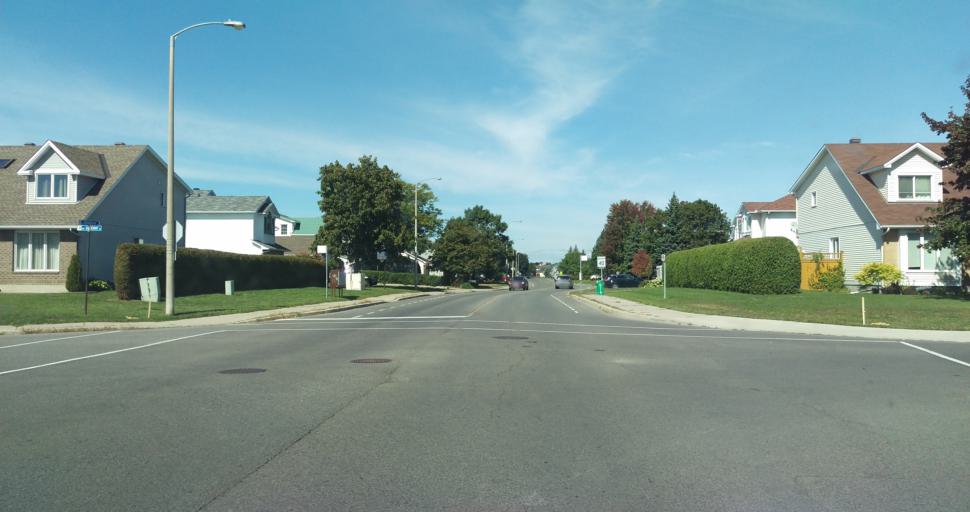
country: CA
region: Ontario
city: Clarence-Rockland
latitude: 45.4664
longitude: -75.4777
